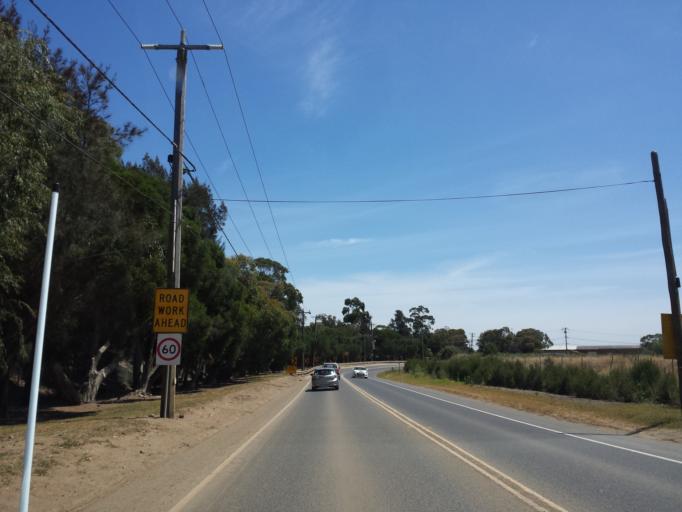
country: AU
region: Victoria
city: Heatherton
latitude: -37.9503
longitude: 145.0981
